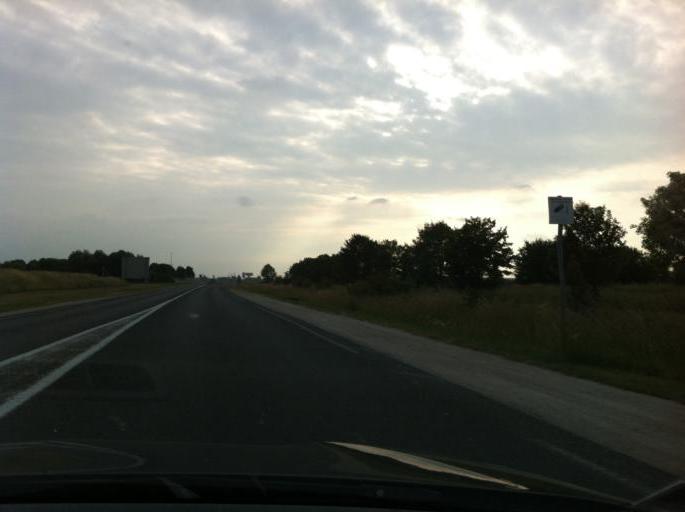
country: FR
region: Ile-de-France
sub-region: Departement de Seine-et-Marne
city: Moissy-Cramayel
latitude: 48.6139
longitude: 2.6295
